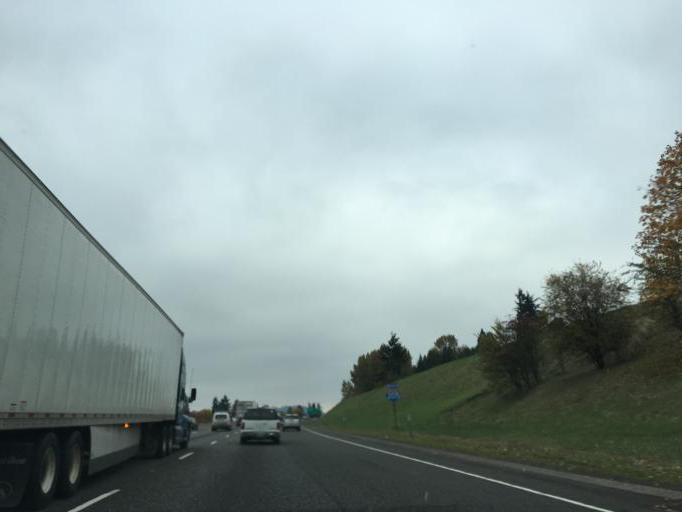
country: US
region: Oregon
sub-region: Multnomah County
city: Lents
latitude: 45.4582
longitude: -122.5723
